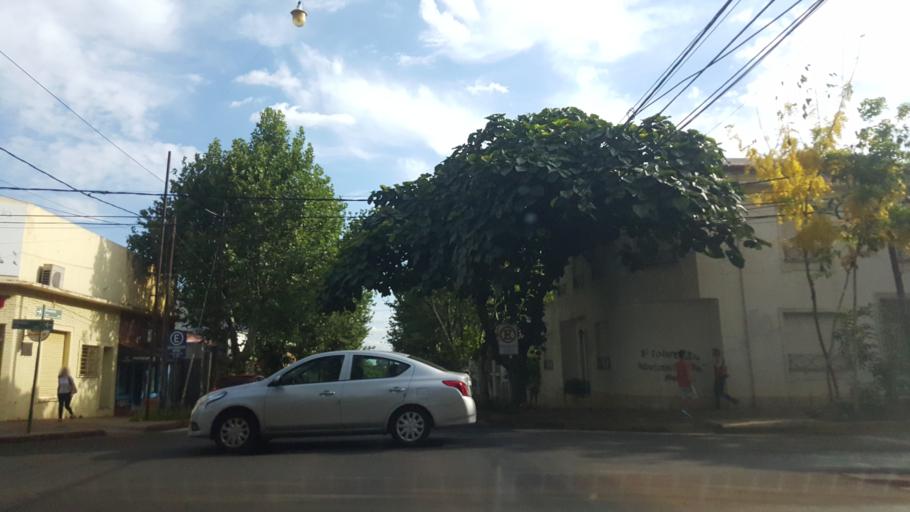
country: AR
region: Misiones
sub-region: Departamento de Capital
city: Posadas
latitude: -27.3680
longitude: -55.8916
